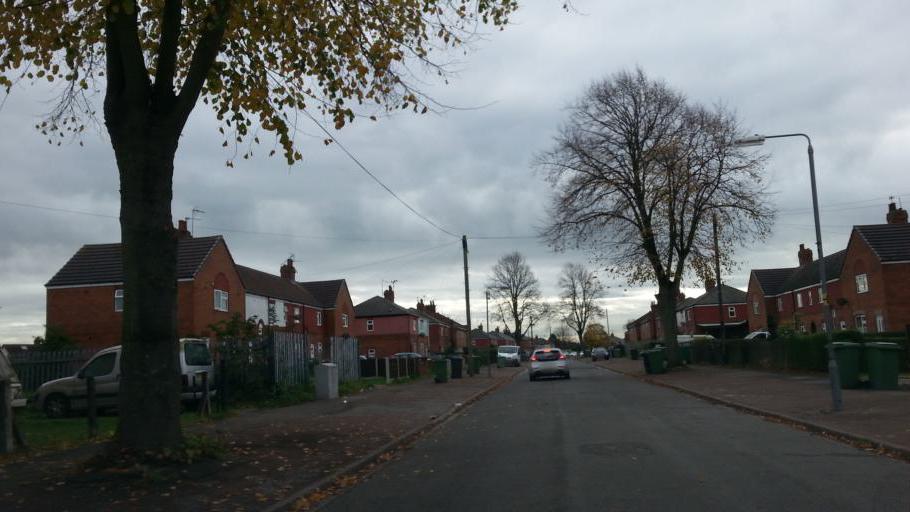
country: GB
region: England
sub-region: Nottinghamshire
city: Newark on Trent
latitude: 53.0658
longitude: -0.8143
